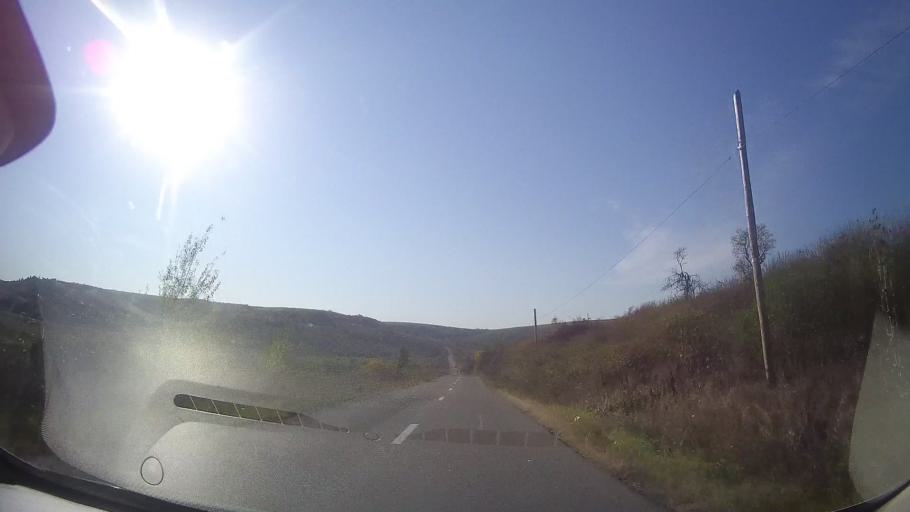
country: RO
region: Timis
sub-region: Oras Recas
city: Recas
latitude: 45.8487
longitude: 21.5189
